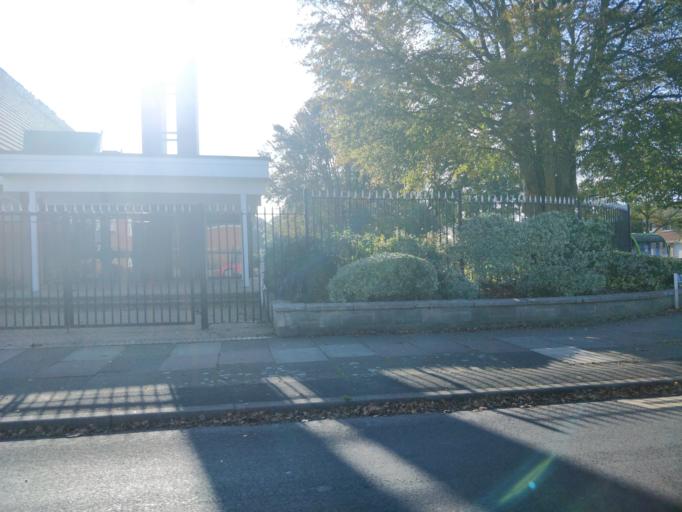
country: GB
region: England
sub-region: Lancashire
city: Banks
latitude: 53.6701
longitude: -2.9571
